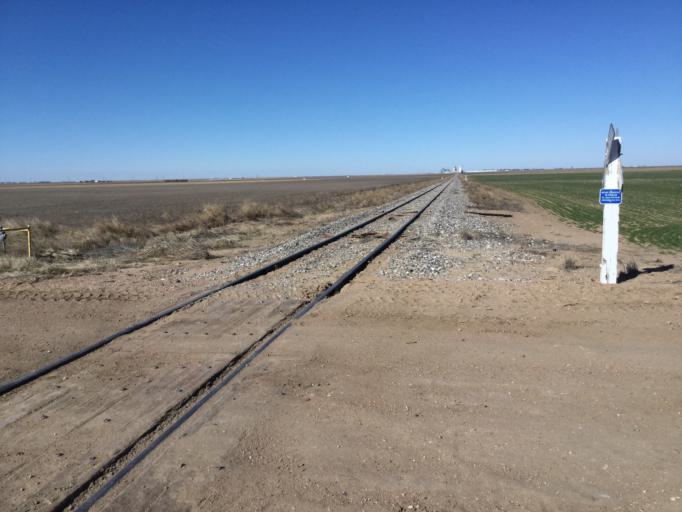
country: US
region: Kansas
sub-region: Grant County
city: Ulysses
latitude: 37.5621
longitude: -101.5082
